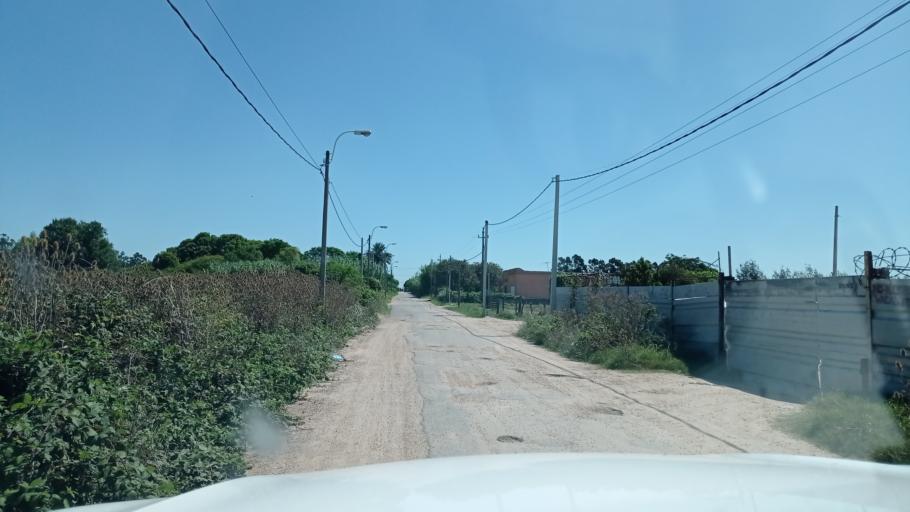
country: UY
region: Montevideo
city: Pajas Blancas
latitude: -34.8694
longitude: -56.2747
